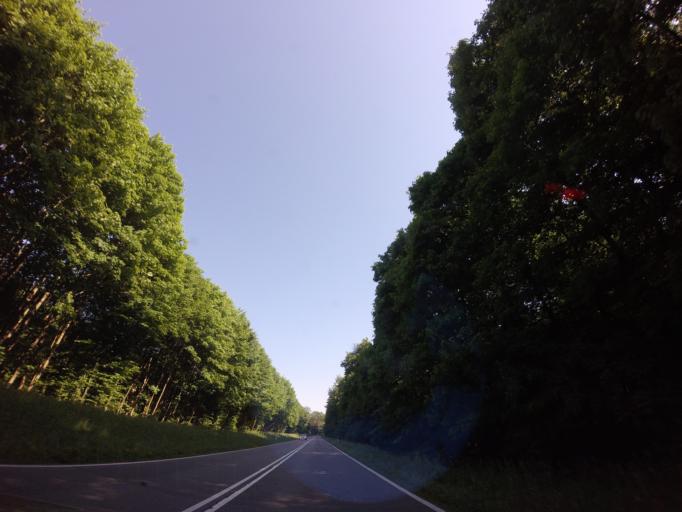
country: PL
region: West Pomeranian Voivodeship
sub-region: Powiat gryfinski
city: Stare Czarnowo
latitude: 53.3280
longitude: 14.7831
